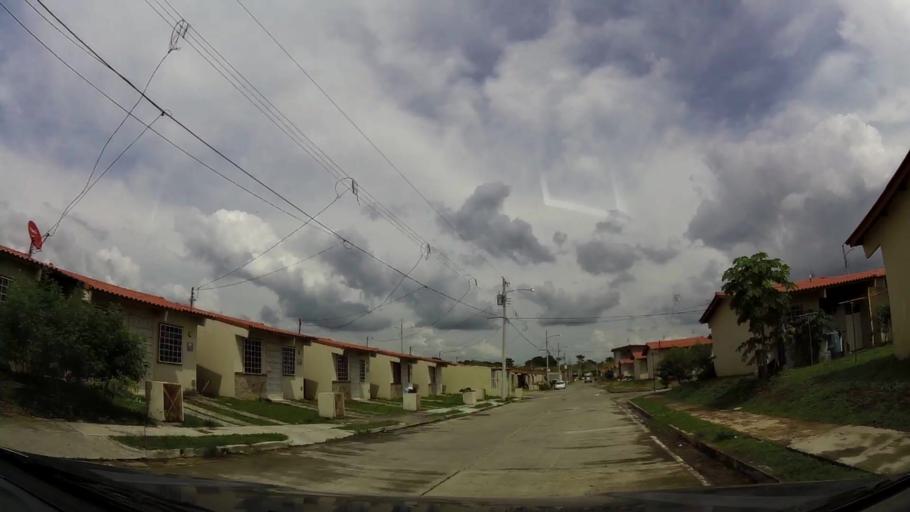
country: PA
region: Panama
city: Cabra Numero Uno
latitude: 9.1206
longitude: -79.3419
